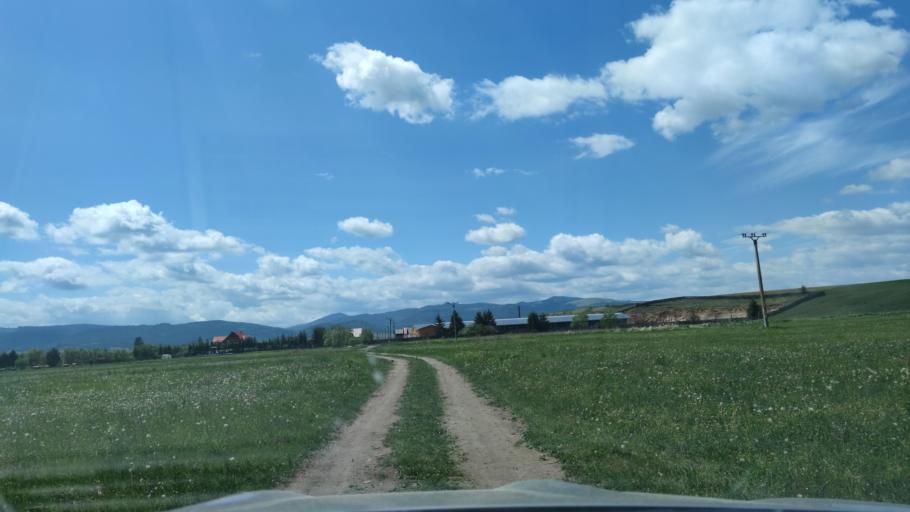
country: RO
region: Harghita
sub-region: Comuna Remetea
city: Remetea
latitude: 46.8137
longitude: 25.4552
